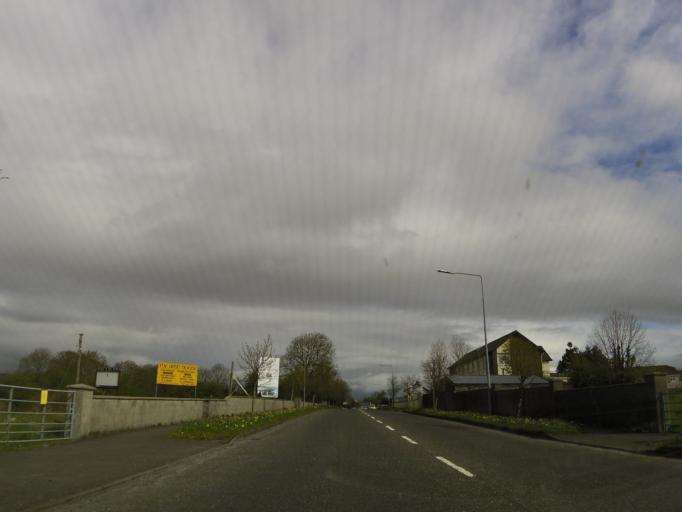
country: IE
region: Connaught
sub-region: Sligo
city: Tobercurry
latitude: 53.9605
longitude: -8.7931
